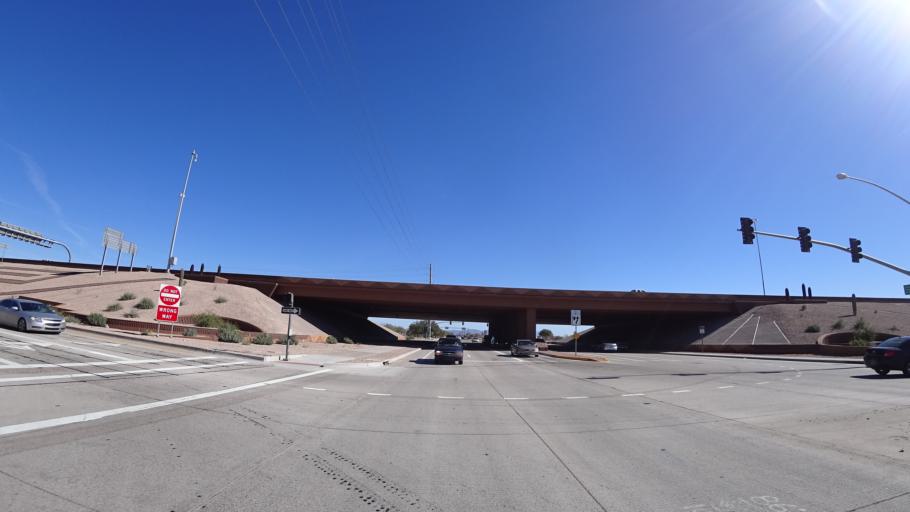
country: US
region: Arizona
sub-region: Maricopa County
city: Scottsdale
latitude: 33.5095
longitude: -111.8887
